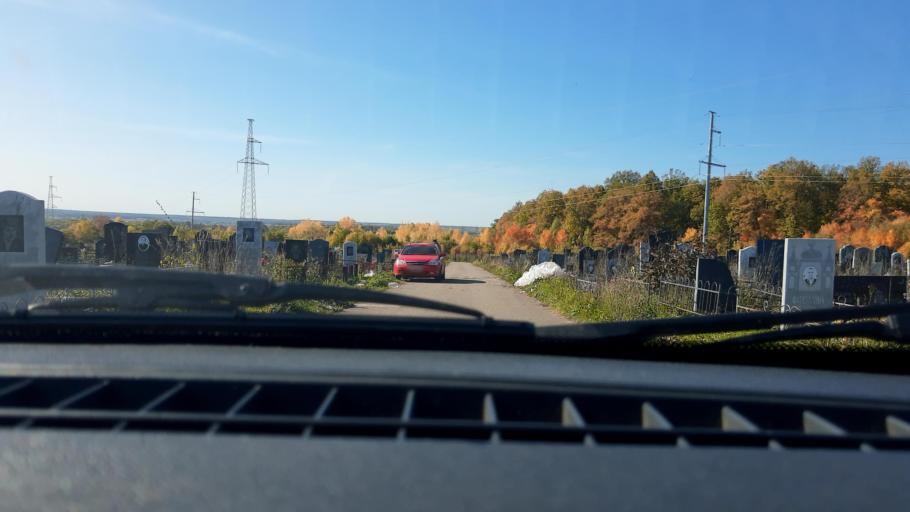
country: RU
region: Bashkortostan
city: Mikhaylovka
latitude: 54.8152
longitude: 55.8600
